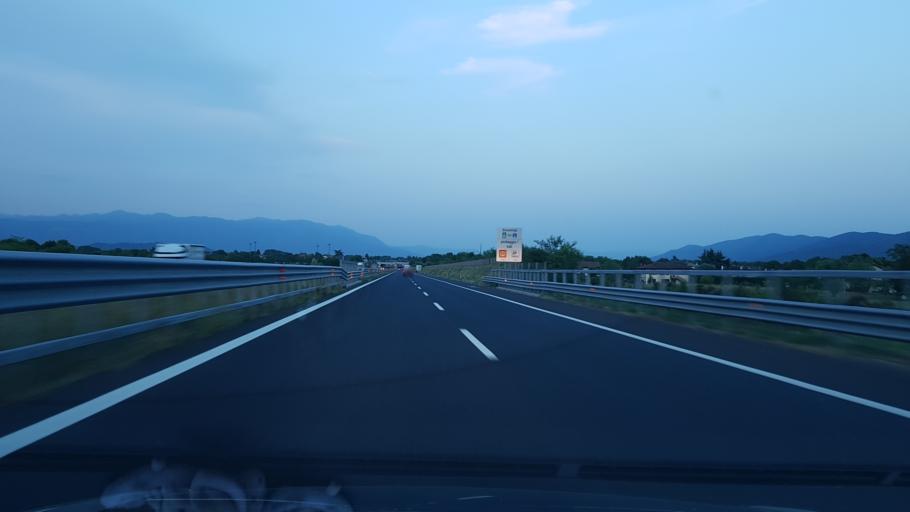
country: IT
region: Friuli Venezia Giulia
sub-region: Provincia di Gorizia
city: Savogna d'Isonzo
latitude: 45.9039
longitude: 13.5614
